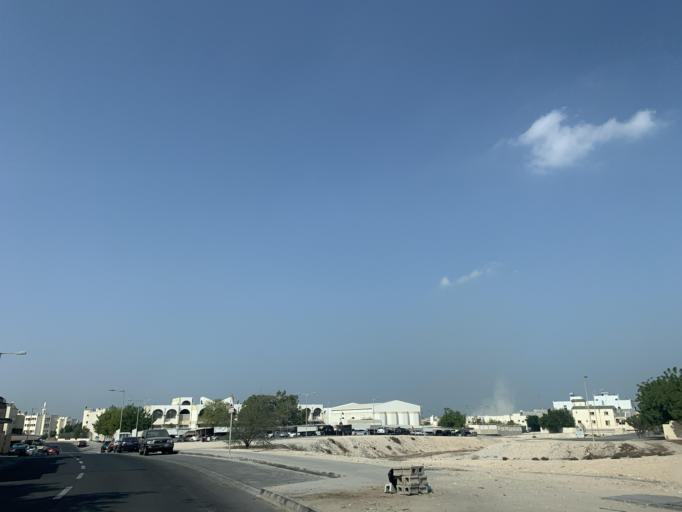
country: BH
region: Central Governorate
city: Madinat Hamad
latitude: 26.1317
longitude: 50.5042
